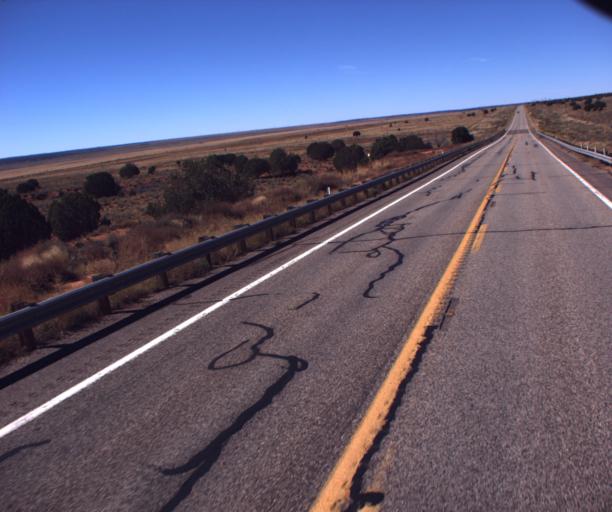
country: US
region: Arizona
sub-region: Mohave County
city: Colorado City
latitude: 36.8581
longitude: -112.7772
